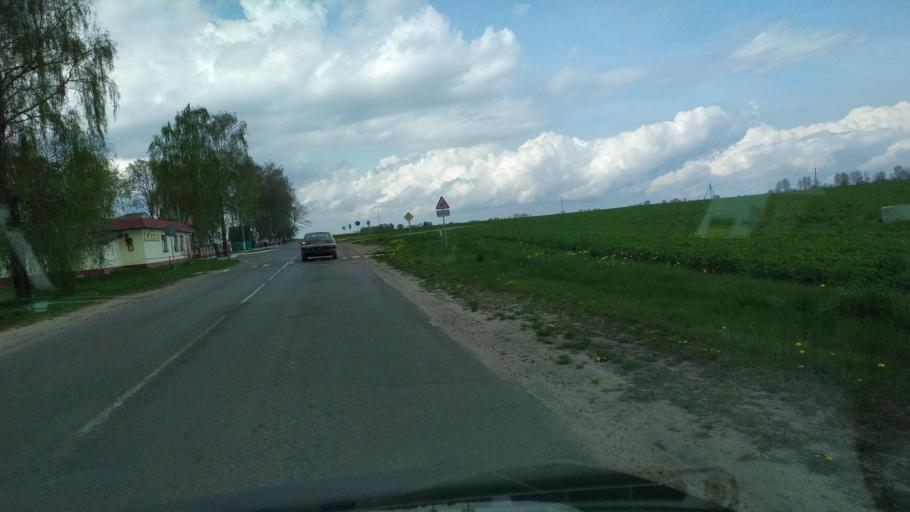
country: BY
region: Brest
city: Pruzhany
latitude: 52.6020
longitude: 24.4018
